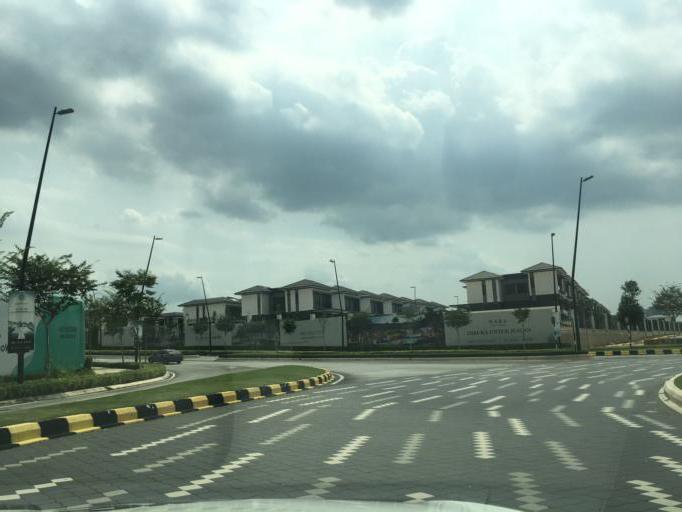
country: MY
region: Selangor
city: Shah Alam
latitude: 3.0961
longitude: 101.4772
